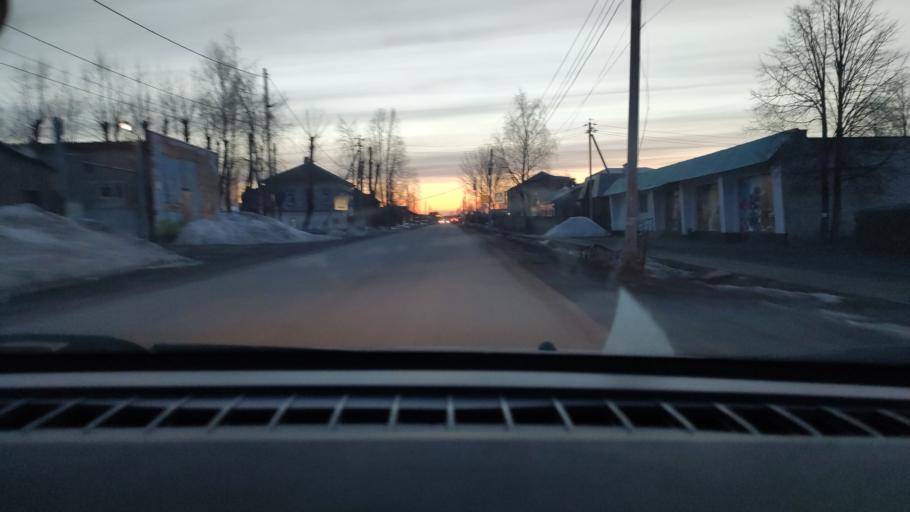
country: RU
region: Perm
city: Yug
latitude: 57.7324
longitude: 56.1753
